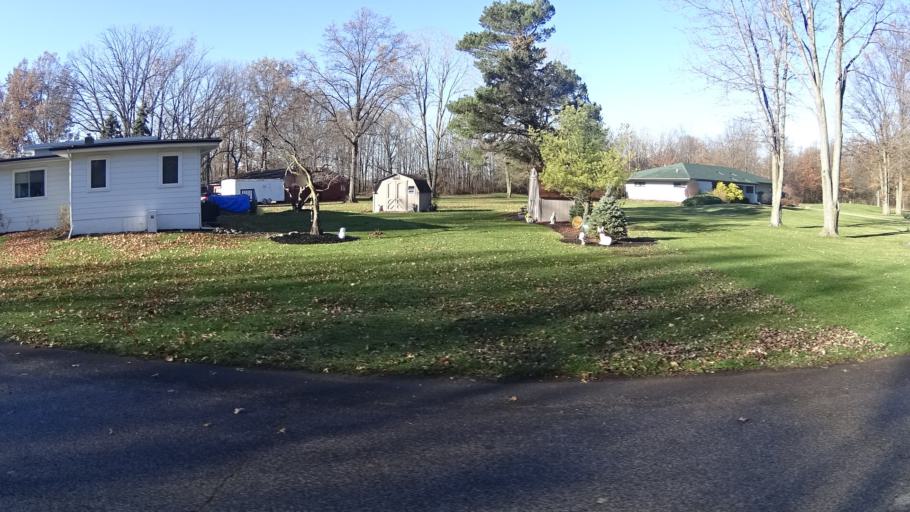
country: US
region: Ohio
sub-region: Lorain County
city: Sheffield Lake
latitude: 41.4624
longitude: -82.1062
